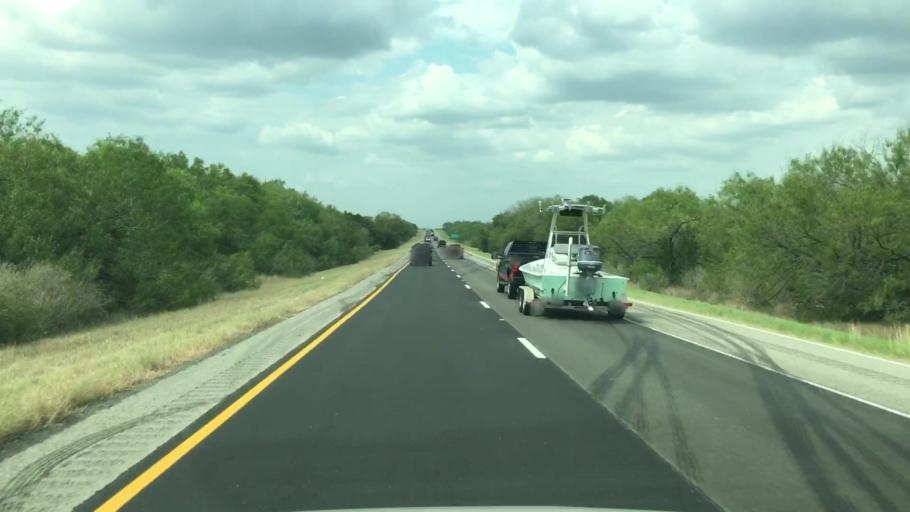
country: US
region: Texas
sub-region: Atascosa County
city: Pleasanton
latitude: 28.9290
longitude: -98.4351
